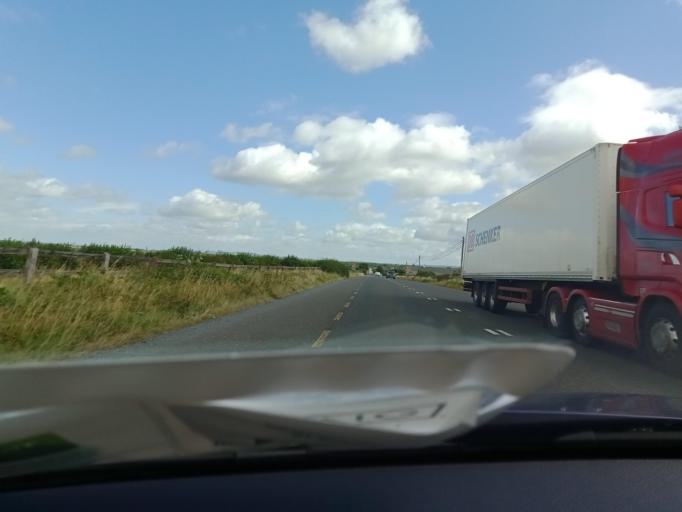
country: IE
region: Leinster
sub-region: Laois
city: Rathdowney
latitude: 52.8267
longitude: -7.4602
